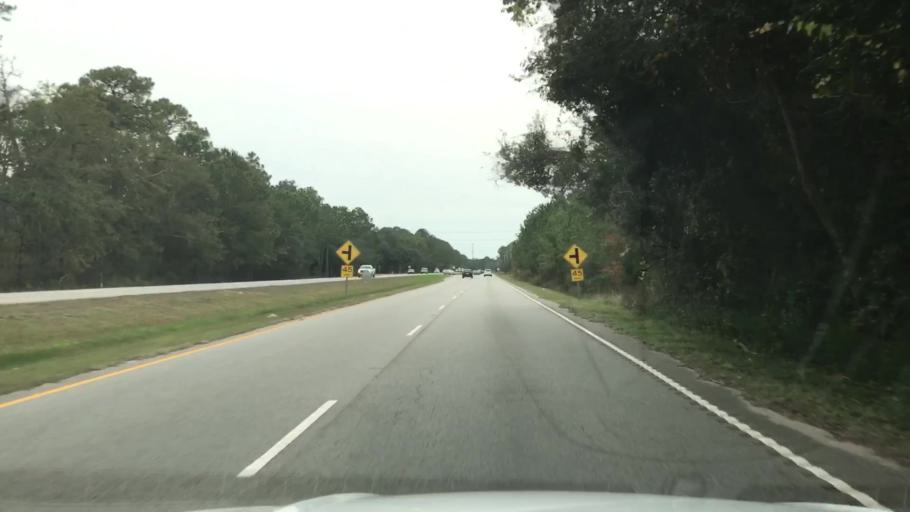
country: US
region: South Carolina
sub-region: Georgetown County
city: Georgetown
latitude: 33.3774
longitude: -79.2123
